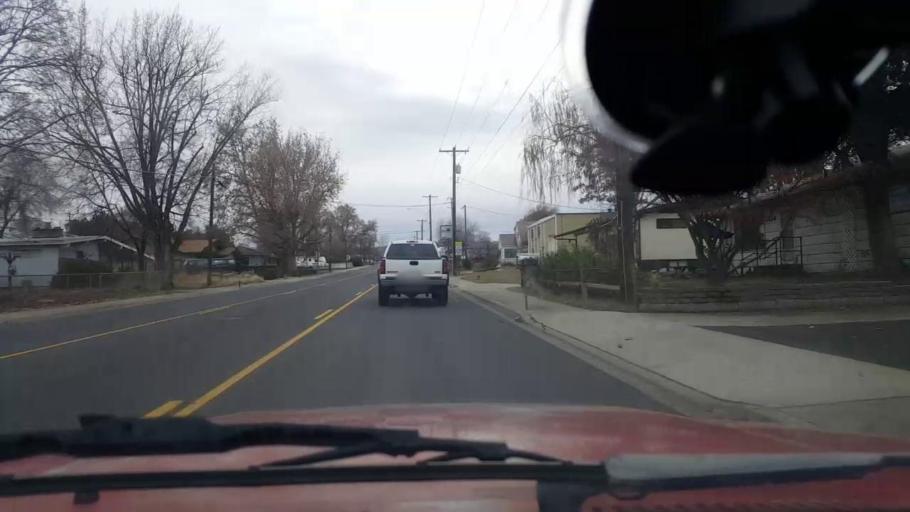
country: US
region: Washington
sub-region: Asotin County
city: West Clarkston-Highland
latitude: 46.4085
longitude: -117.0691
